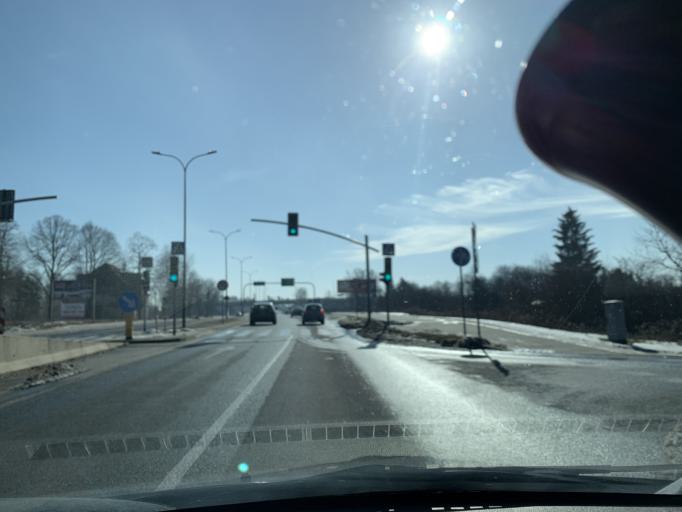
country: PL
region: Silesian Voivodeship
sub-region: Powiat tarnogorski
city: Radzionkow
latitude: 50.3707
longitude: 18.8947
